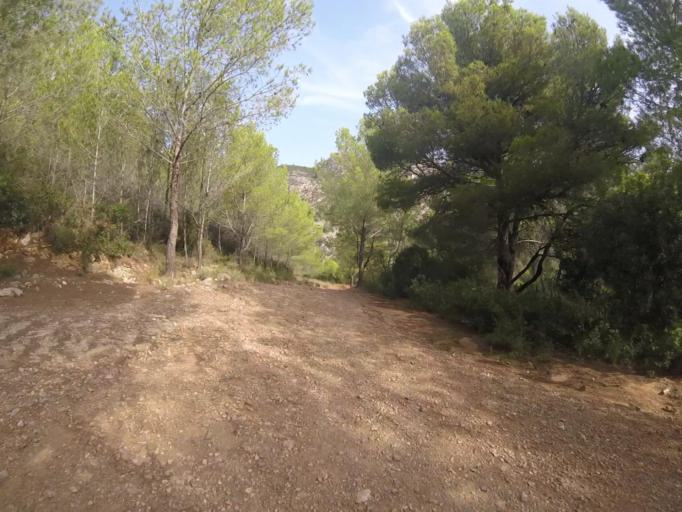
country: ES
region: Valencia
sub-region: Provincia de Castello
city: Benicassim
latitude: 40.0877
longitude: 0.0481
